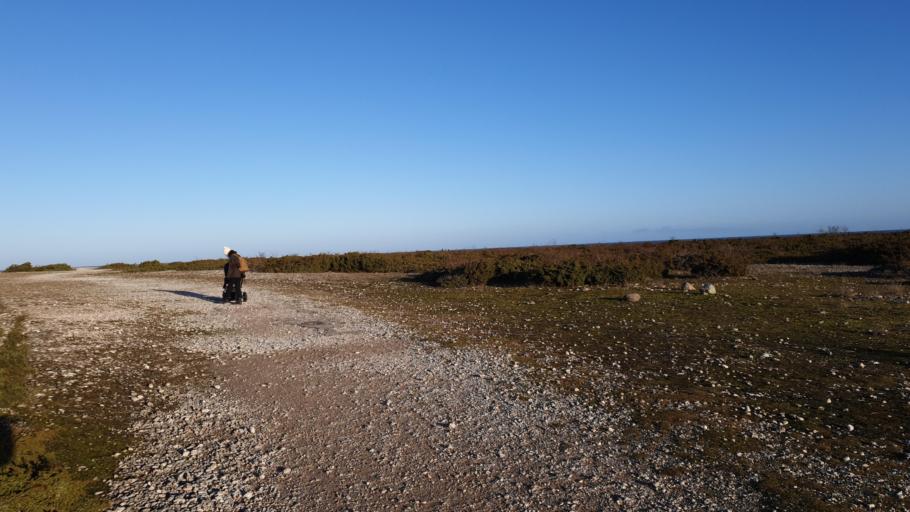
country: SE
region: Gotland
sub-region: Gotland
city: Slite
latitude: 57.9966
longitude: 19.1810
